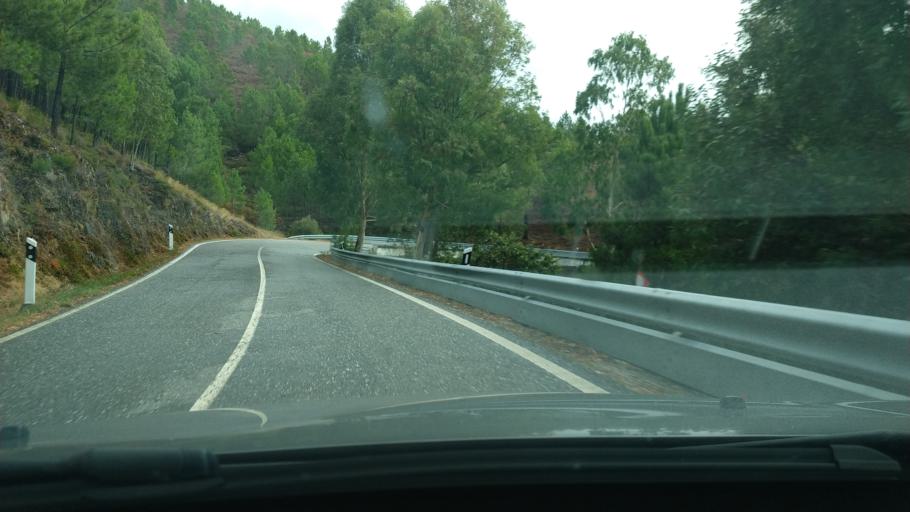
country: PT
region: Castelo Branco
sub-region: Covilha
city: Covilha
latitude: 40.2361
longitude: -7.6668
